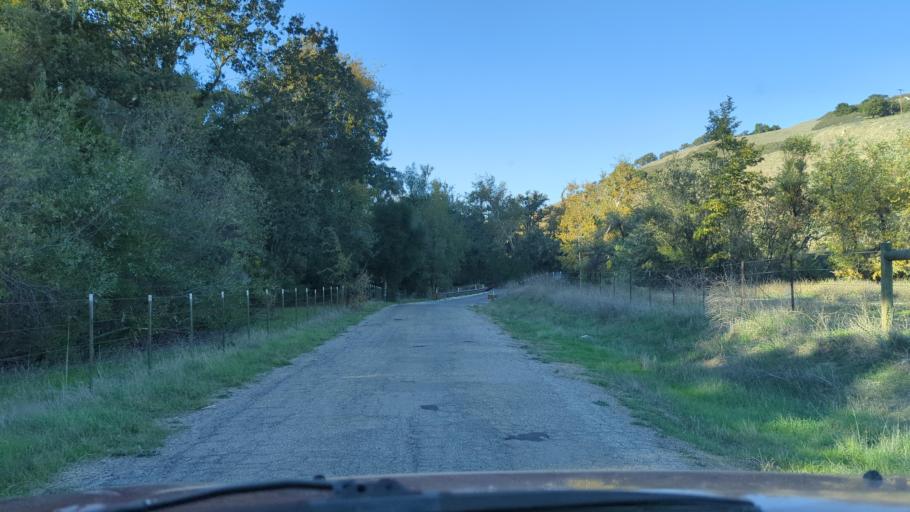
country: US
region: California
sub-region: Santa Barbara County
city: Santa Ynez
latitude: 34.5575
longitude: -120.0833
